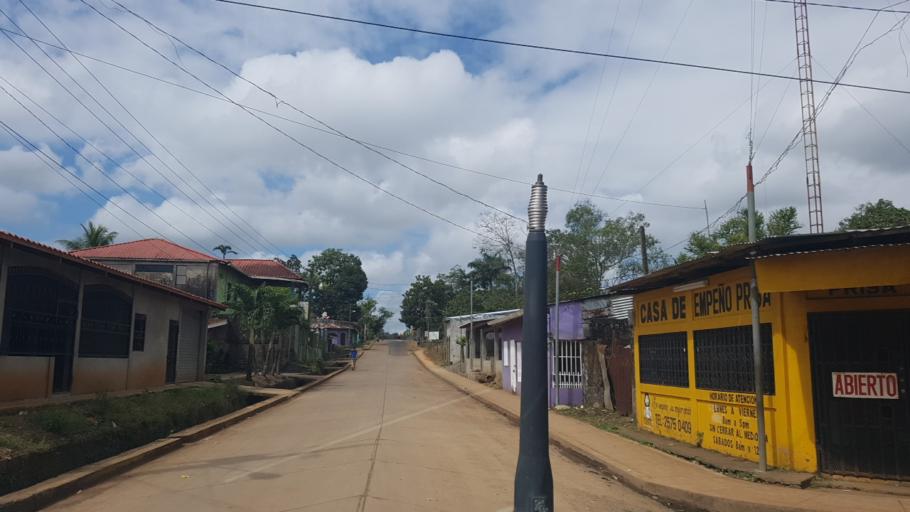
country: NI
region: Atlantico Sur
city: Nueva Guinea
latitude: 11.6896
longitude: -84.4558
